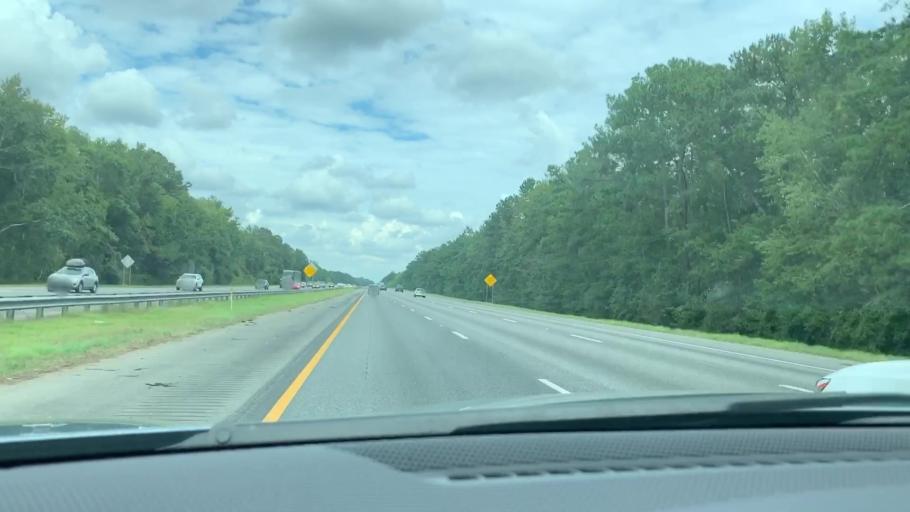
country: US
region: Georgia
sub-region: Bryan County
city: Richmond Hill
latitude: 31.9755
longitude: -81.3132
